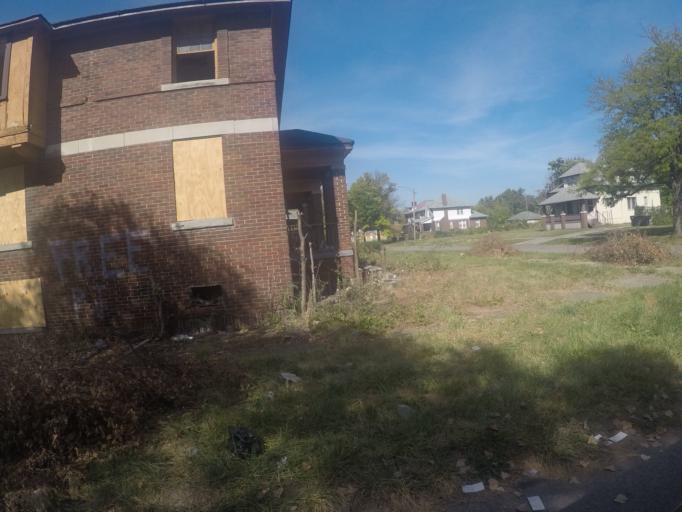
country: US
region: Michigan
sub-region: Wayne County
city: Highland Park
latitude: 42.3614
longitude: -83.1314
